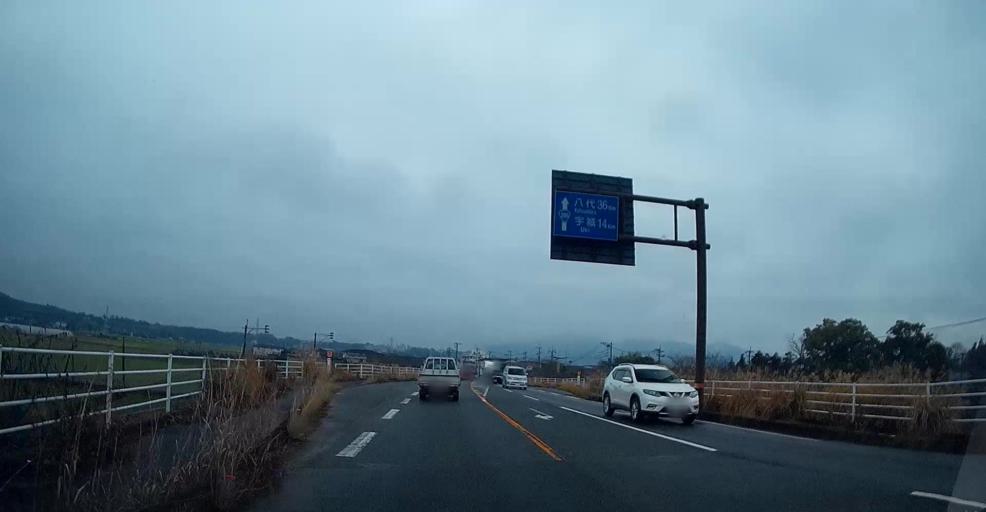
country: JP
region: Kumamoto
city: Kumamoto
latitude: 32.7331
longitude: 130.7388
